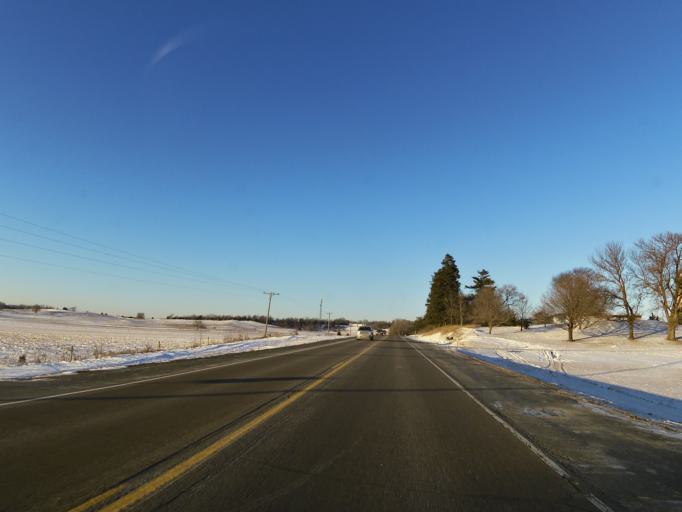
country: US
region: Minnesota
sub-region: Dakota County
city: Farmington
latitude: 44.5509
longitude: -93.1367
